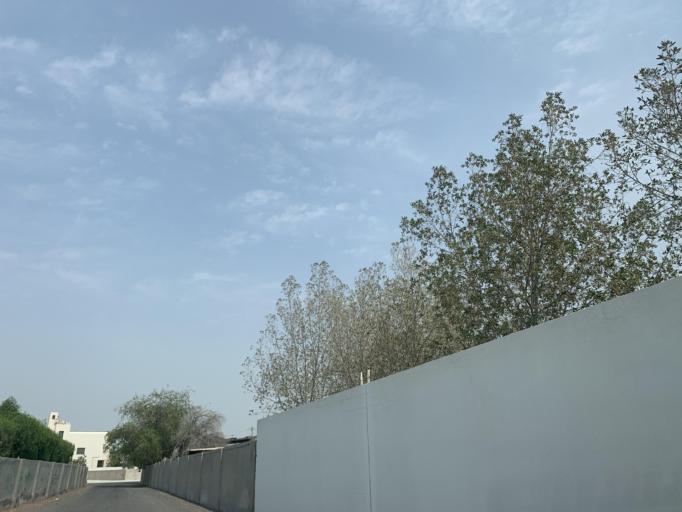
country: BH
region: Manama
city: Jidd Hafs
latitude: 26.2164
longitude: 50.4863
